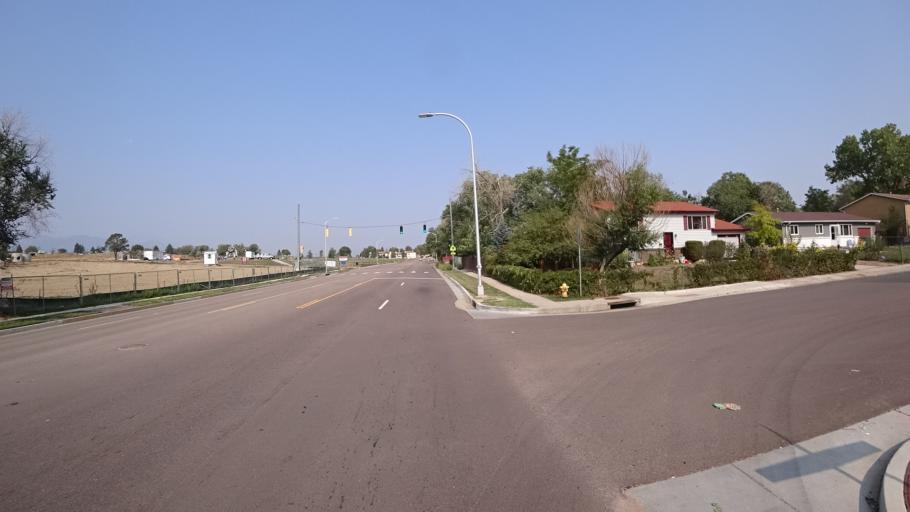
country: US
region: Colorado
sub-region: El Paso County
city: Stratmoor
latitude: 38.8075
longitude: -104.7635
